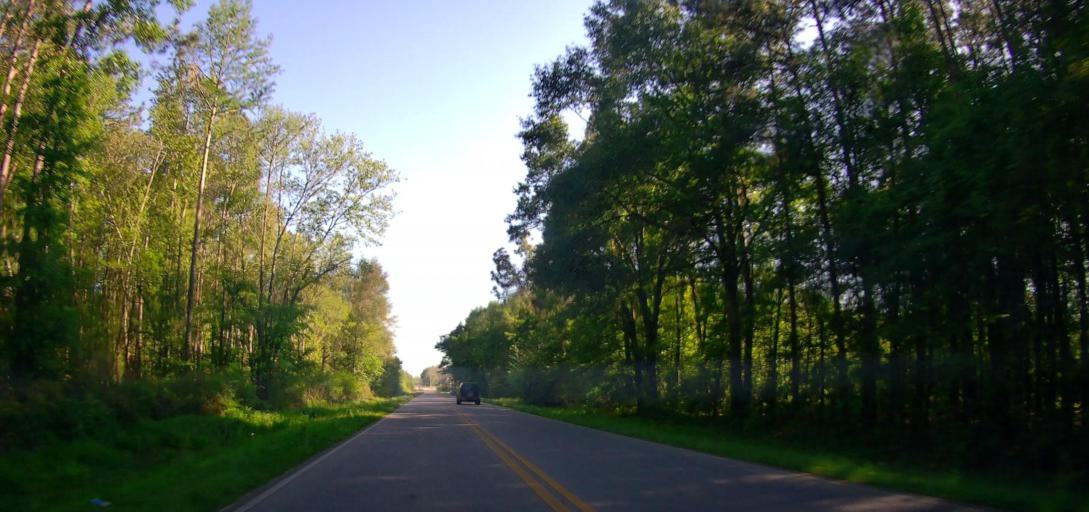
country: US
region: Georgia
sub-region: Ben Hill County
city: Fitzgerald
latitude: 31.7187
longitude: -83.2356
